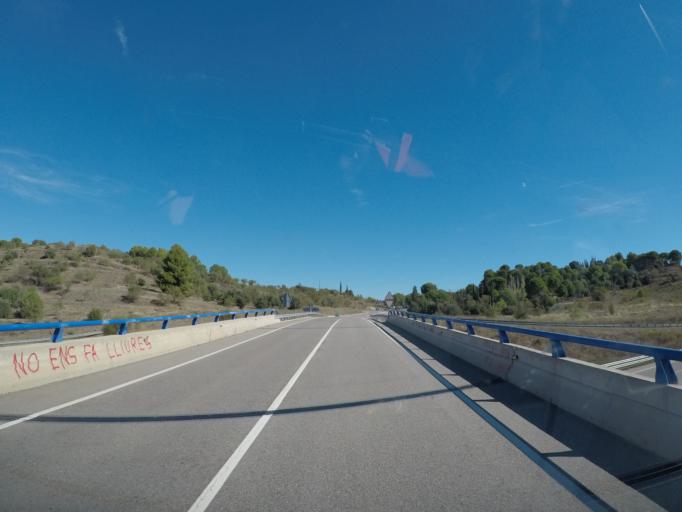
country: ES
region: Catalonia
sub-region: Provincia de Tarragona
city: Falset
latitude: 41.1403
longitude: 0.8093
